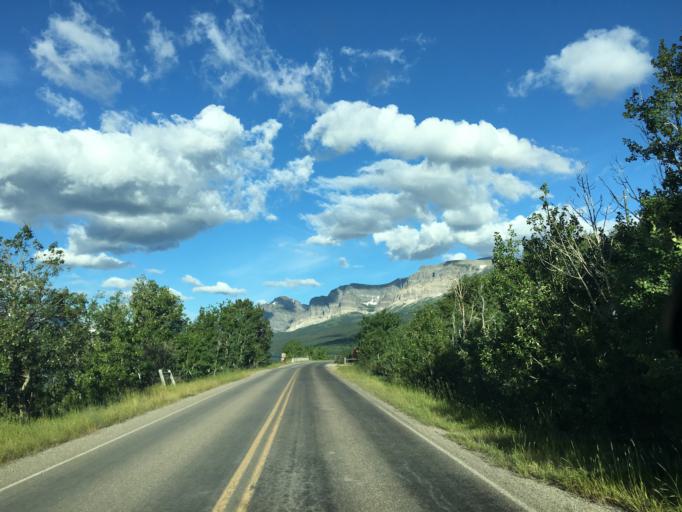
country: CA
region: Alberta
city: Cardston
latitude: 48.8299
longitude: -113.5233
